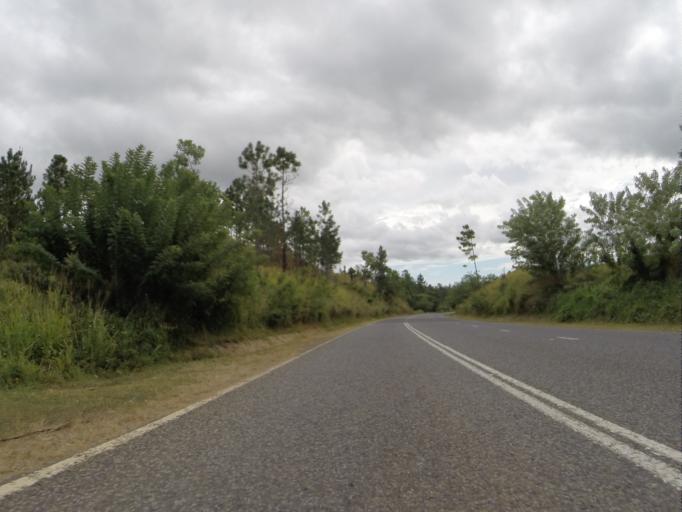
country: FJ
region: Western
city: Nadi
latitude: -18.0193
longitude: 177.3283
